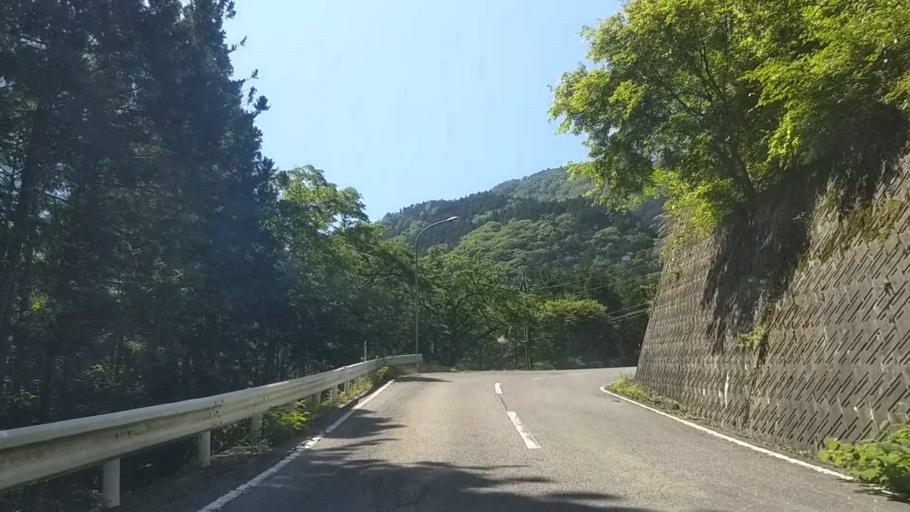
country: JP
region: Yamanashi
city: Ryuo
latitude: 35.5099
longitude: 138.4050
